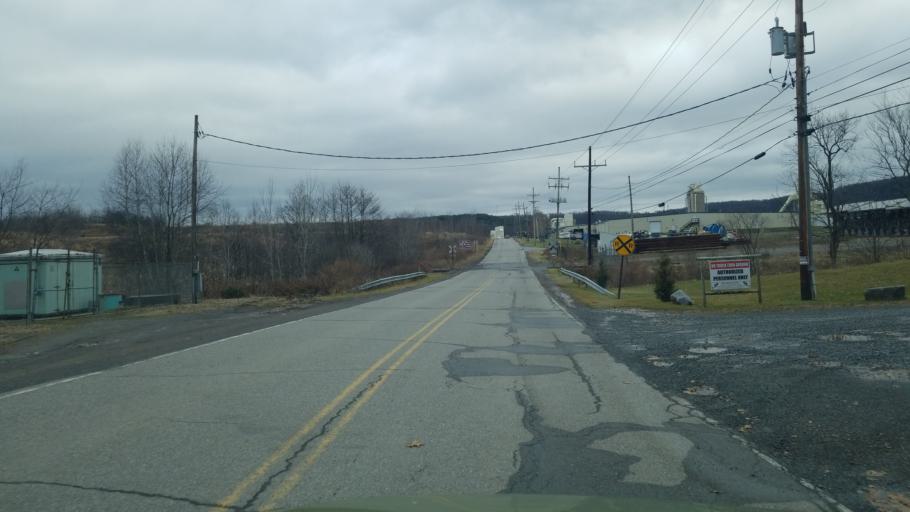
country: US
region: Pennsylvania
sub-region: Clearfield County
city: Clearfield
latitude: 41.0285
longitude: -78.3985
